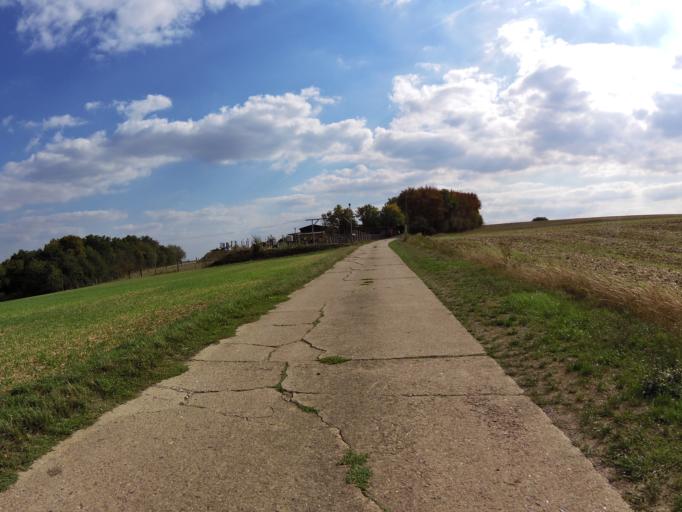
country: DE
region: Bavaria
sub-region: Regierungsbezirk Unterfranken
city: Hettstadt
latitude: 49.7917
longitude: 9.7956
